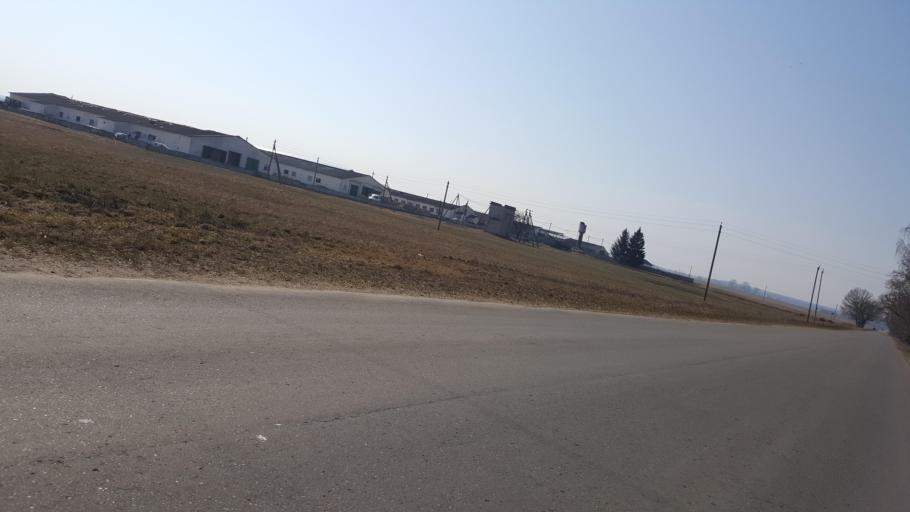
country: BY
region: Brest
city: Kamyanyets
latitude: 52.3158
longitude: 23.9141
